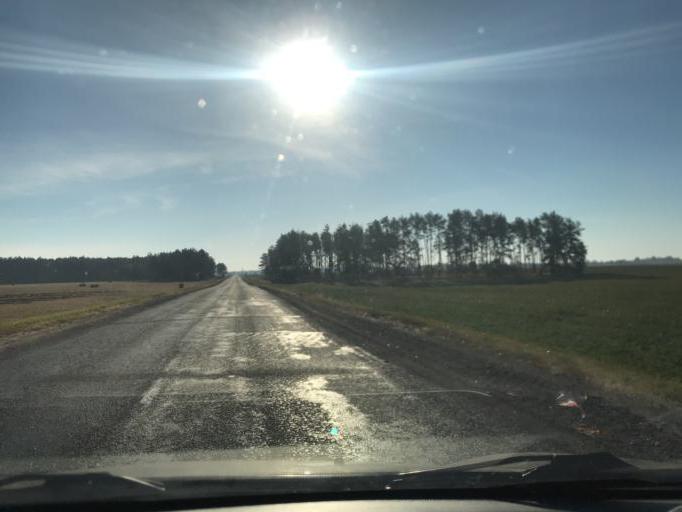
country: BY
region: Gomel
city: Khoyniki
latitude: 51.8155
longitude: 30.0929
